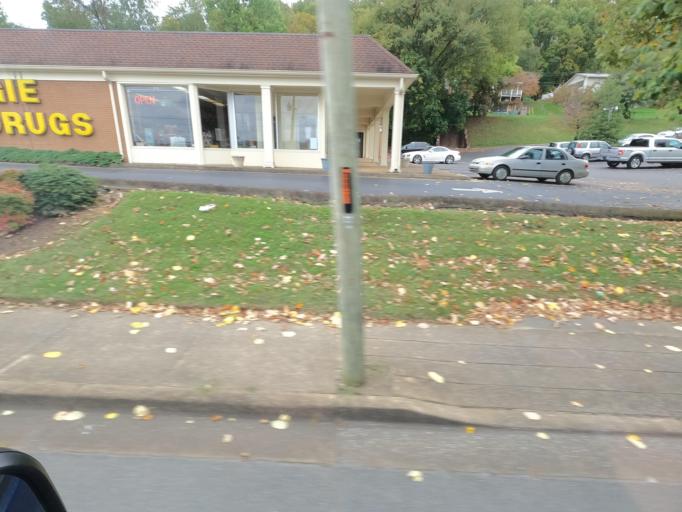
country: US
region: Tennessee
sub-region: Carter County
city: Elizabethton
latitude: 36.3429
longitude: -82.2406
